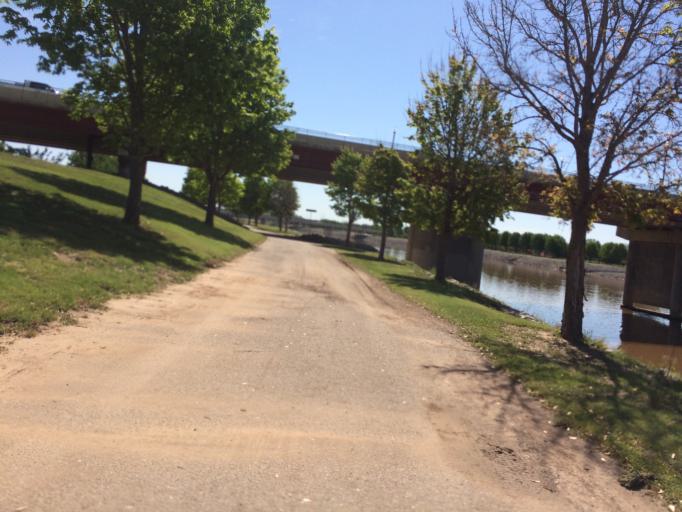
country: US
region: Oklahoma
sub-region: Oklahoma County
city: Oklahoma City
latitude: 35.4492
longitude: -97.5219
